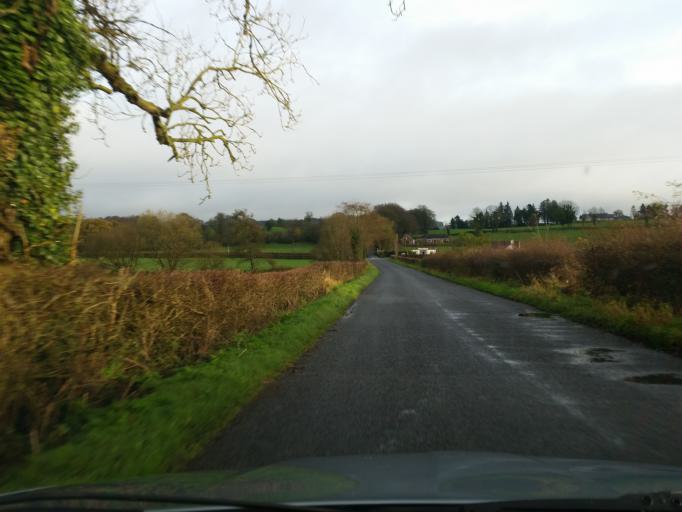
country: GB
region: Northern Ireland
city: Lisnaskea
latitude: 54.2843
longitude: -7.4299
